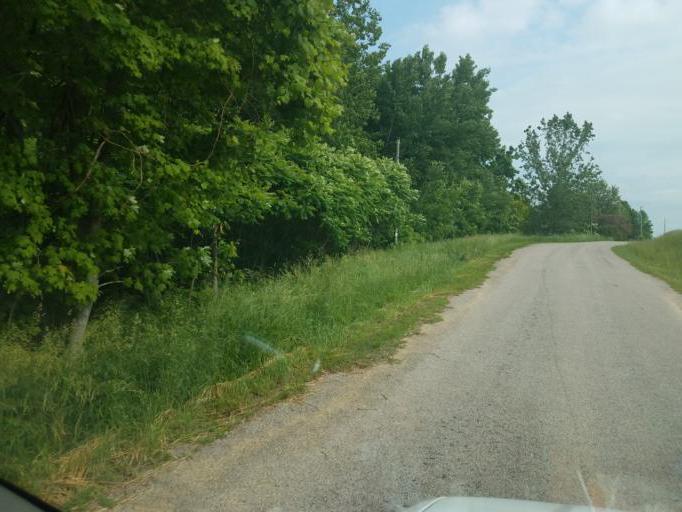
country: US
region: Wisconsin
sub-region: Vernon County
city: Hillsboro
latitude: 43.5951
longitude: -90.4165
